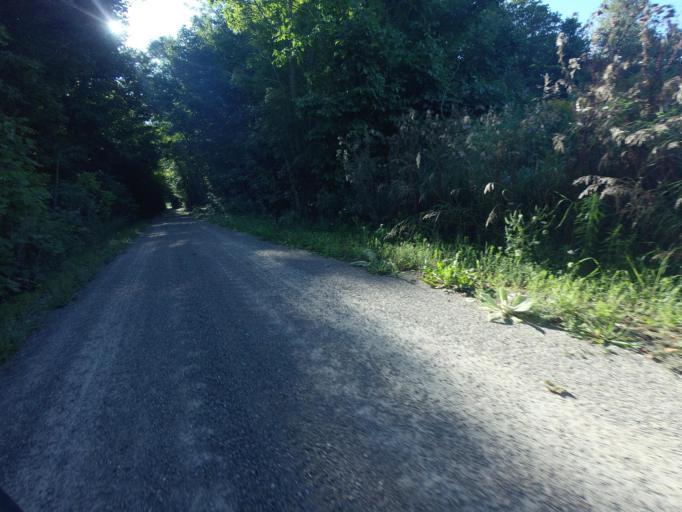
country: CA
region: Ontario
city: Huron East
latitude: 43.7418
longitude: -81.4805
